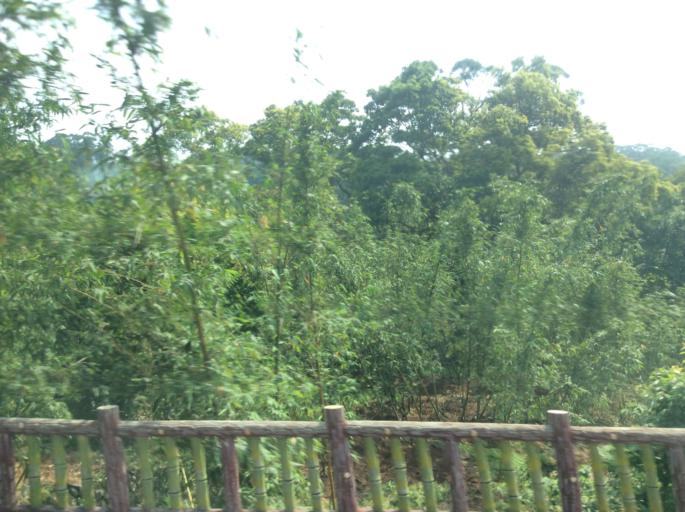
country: TW
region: Taipei
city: Taipei
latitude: 25.1262
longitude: 121.5495
